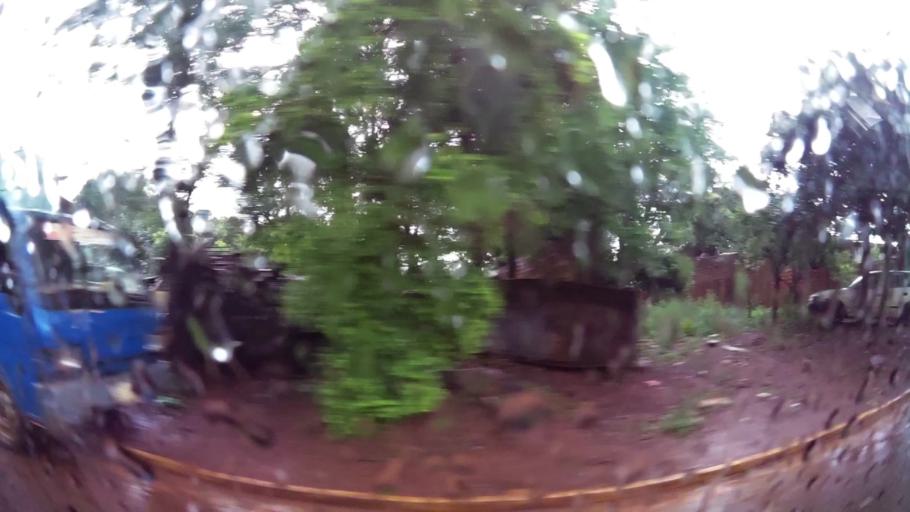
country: PY
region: Alto Parana
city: Presidente Franco
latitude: -25.5395
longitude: -54.6782
